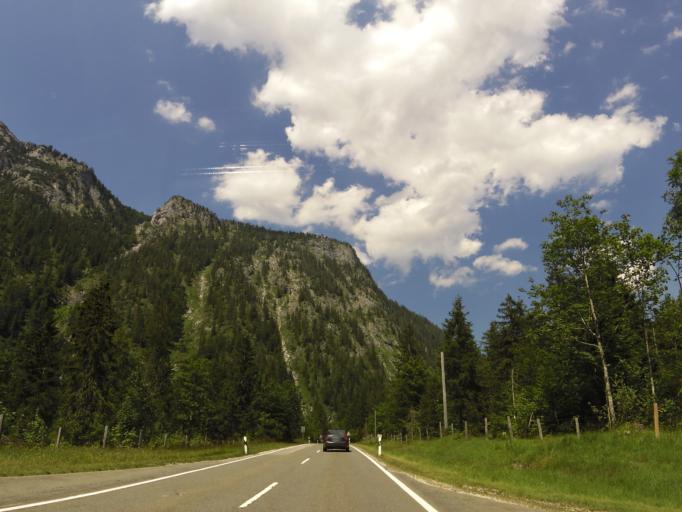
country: DE
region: Bavaria
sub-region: Upper Bavaria
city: Ruhpolding
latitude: 47.6942
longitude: 12.6027
